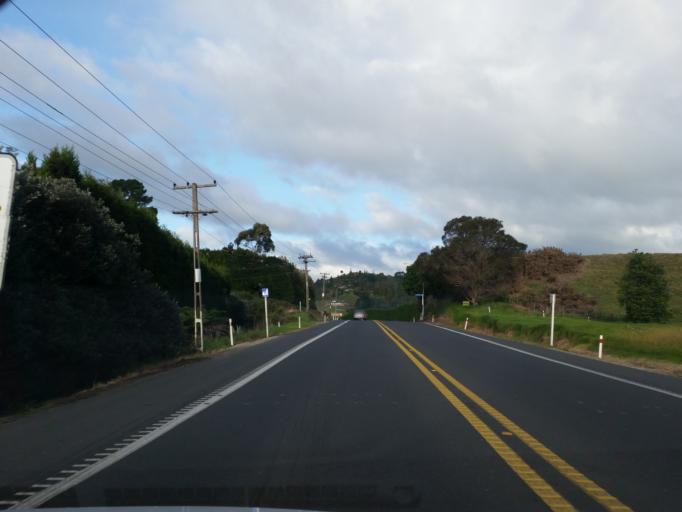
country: NZ
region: Bay of Plenty
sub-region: Tauranga City
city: Tauranga
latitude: -37.6944
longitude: 176.0486
